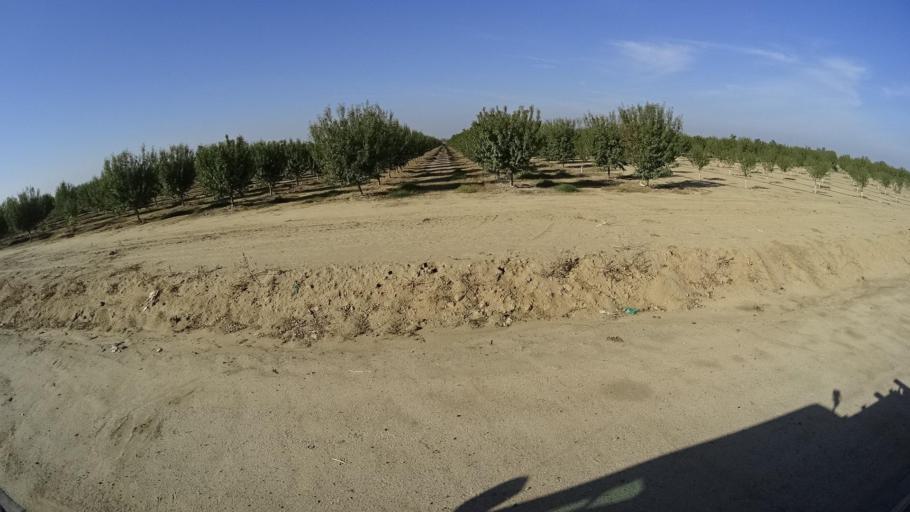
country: US
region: California
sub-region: Kern County
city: Lamont
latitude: 35.3269
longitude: -118.8964
